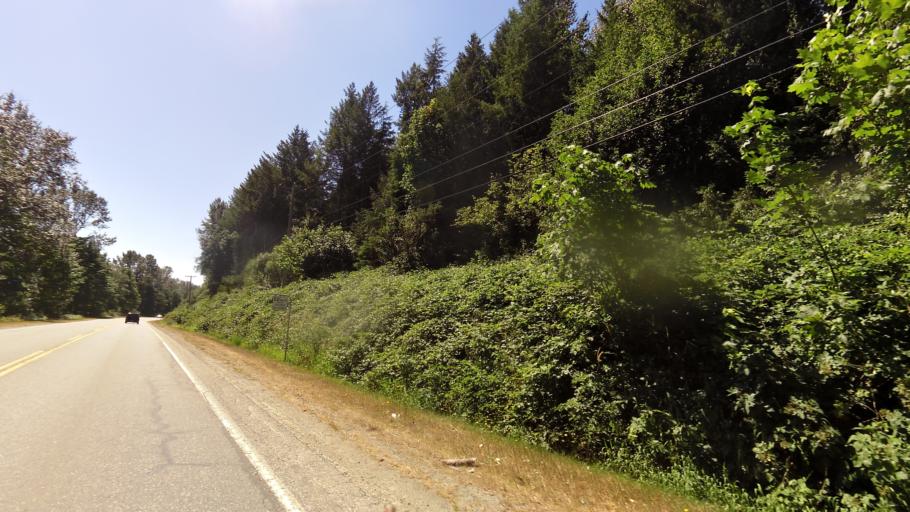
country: CA
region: British Columbia
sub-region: Fraser Valley Regional District
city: Chilliwack
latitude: 49.2073
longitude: -122.0218
